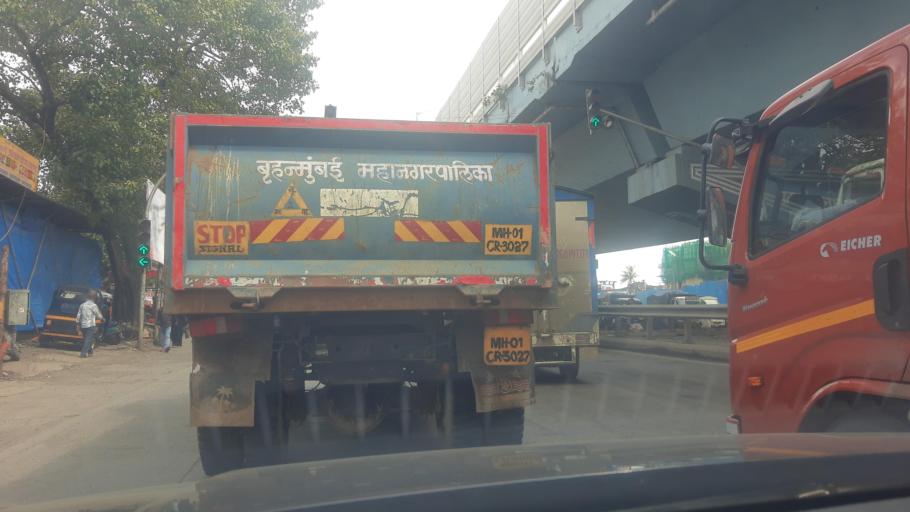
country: IN
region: Maharashtra
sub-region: Mumbai Suburban
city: Mumbai
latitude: 19.0597
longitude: 72.9194
